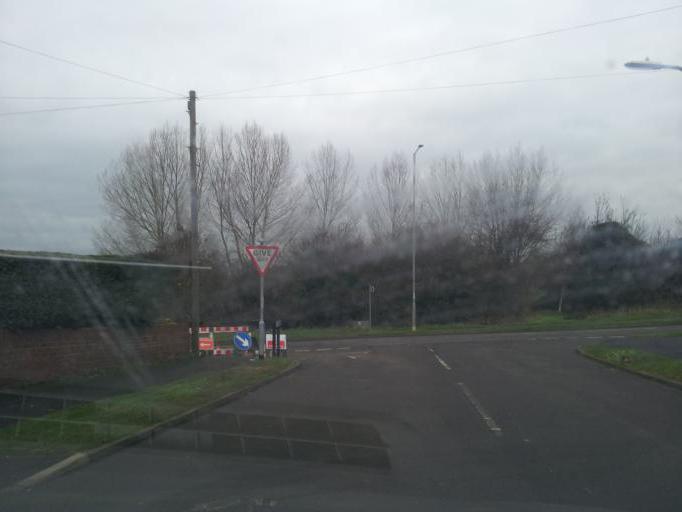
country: GB
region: England
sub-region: Northamptonshire
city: Kettering
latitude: 52.3968
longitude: -0.7010
